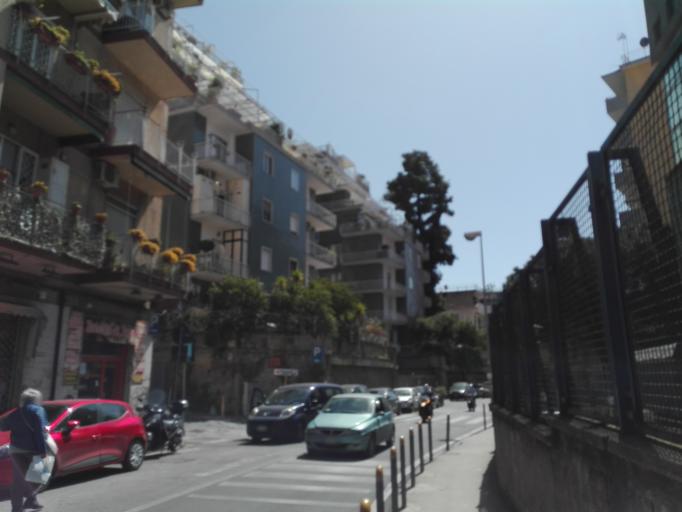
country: IT
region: Campania
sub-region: Provincia di Napoli
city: Napoli
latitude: 40.8536
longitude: 14.2244
